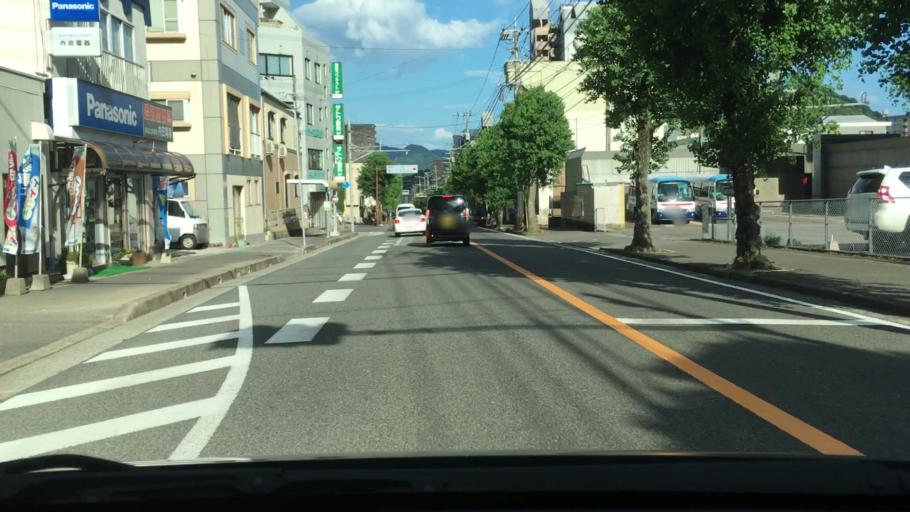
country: JP
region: Nagasaki
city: Togitsu
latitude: 32.8089
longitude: 129.8310
